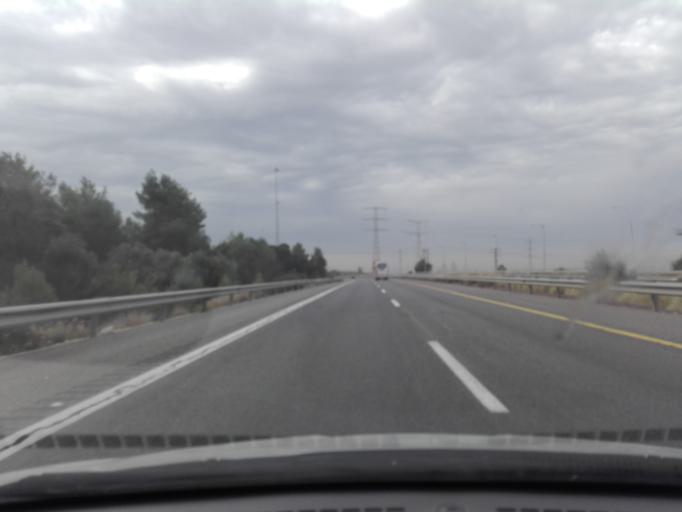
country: IL
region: Central District
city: Lod
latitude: 31.9538
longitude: 34.9333
